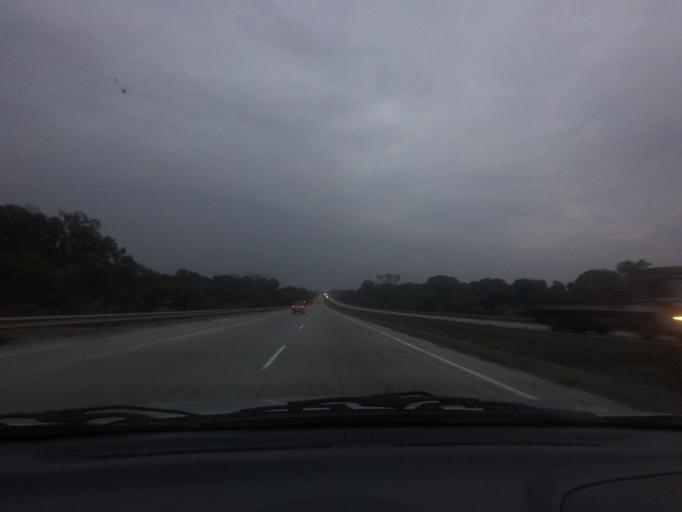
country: IN
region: Karnataka
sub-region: Bangalore Urban
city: Bangalore
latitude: 12.8906
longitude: 77.4820
